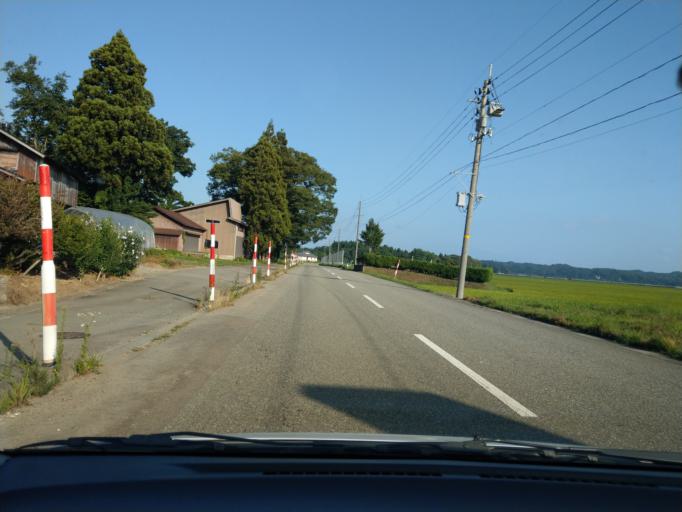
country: JP
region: Akita
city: Akita
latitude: 39.5349
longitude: 140.2545
